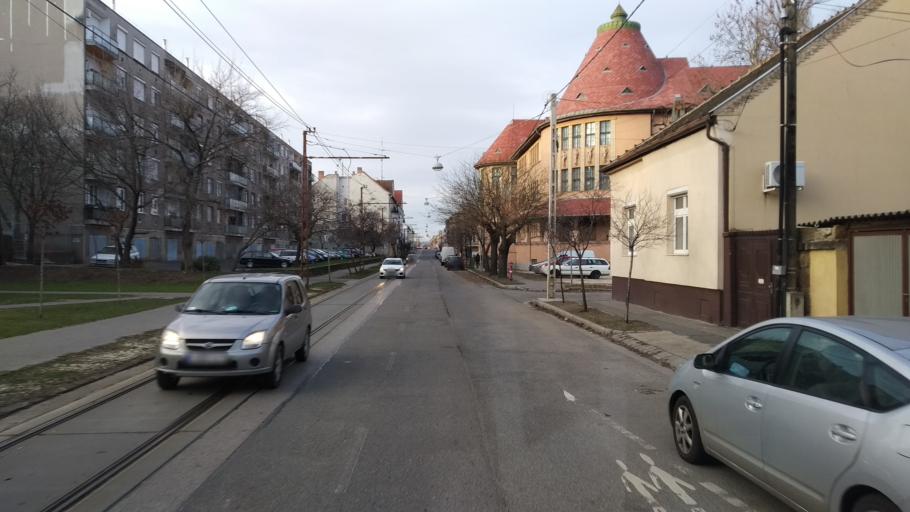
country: HU
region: Budapest
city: Budapest XX. keruelet
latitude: 47.4370
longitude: 19.1085
